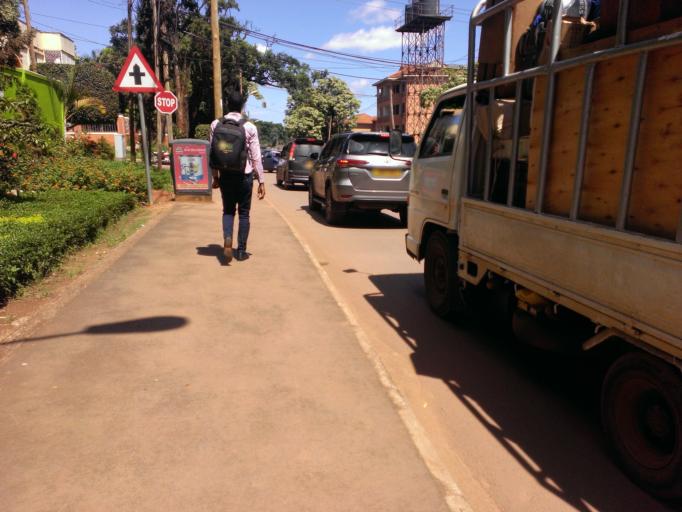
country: UG
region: Central Region
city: Kampala Central Division
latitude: 0.3205
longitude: 32.5781
